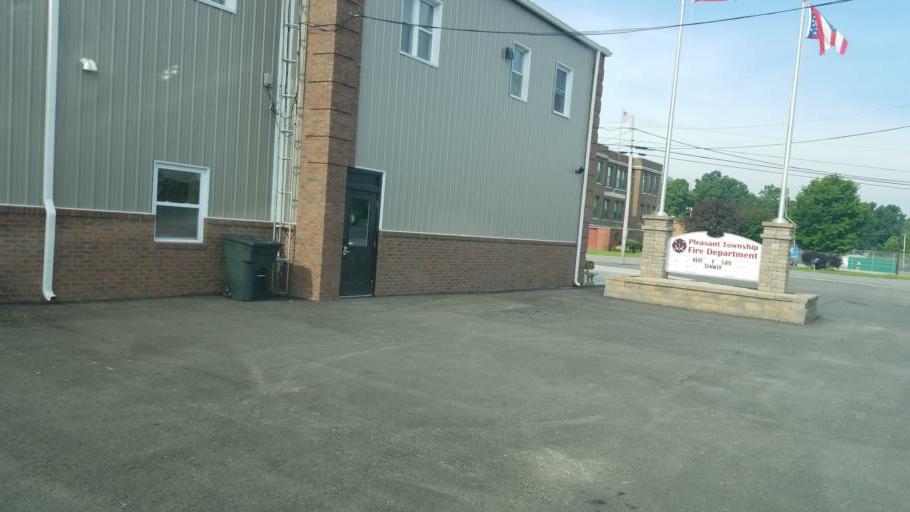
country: US
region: Ohio
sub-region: Marion County
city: Marion
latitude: 40.5202
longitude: -83.1352
